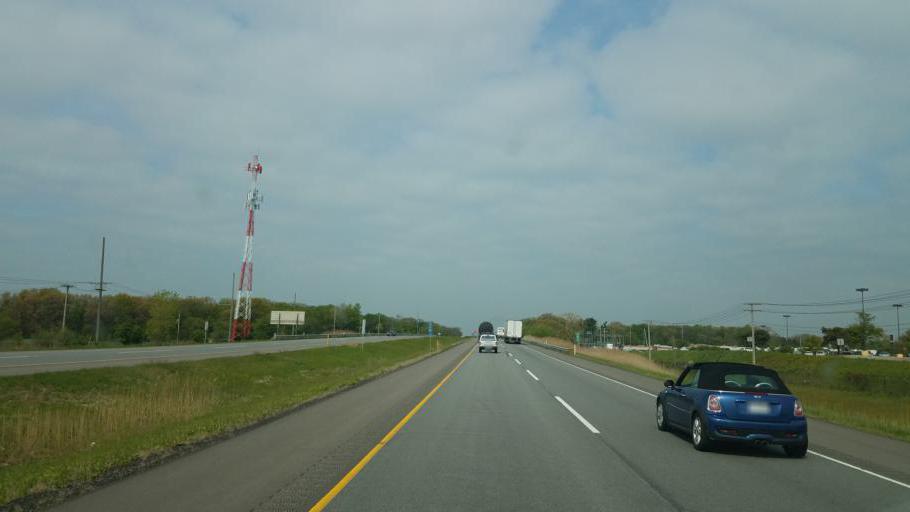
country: US
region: Indiana
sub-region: Saint Joseph County
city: Georgetown
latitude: 41.7163
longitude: -86.1907
